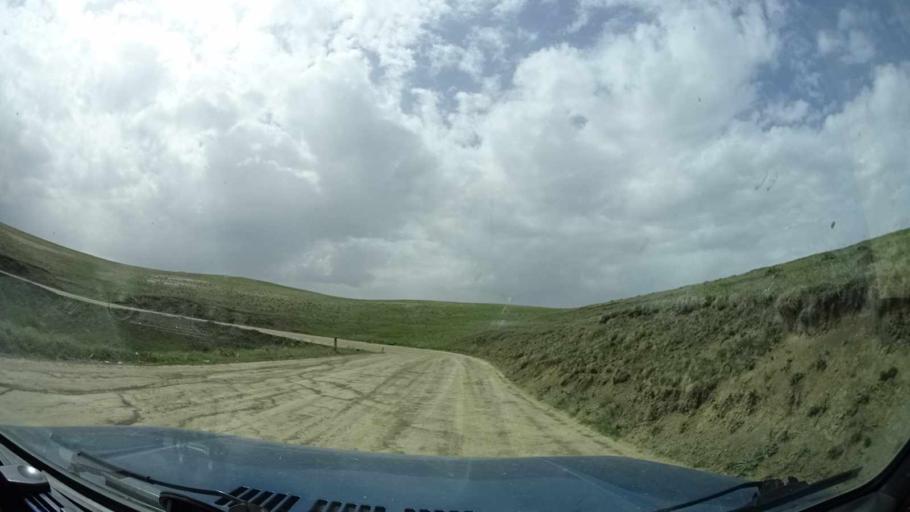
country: RU
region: Dagestan
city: Kubachi
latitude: 42.0843
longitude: 47.5575
